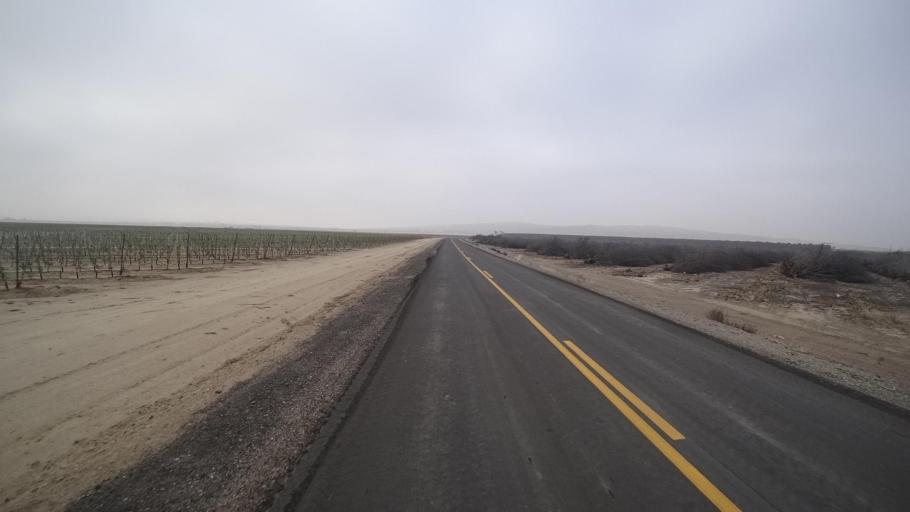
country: US
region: California
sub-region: Kern County
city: Maricopa
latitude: 35.1143
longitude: -119.3519
